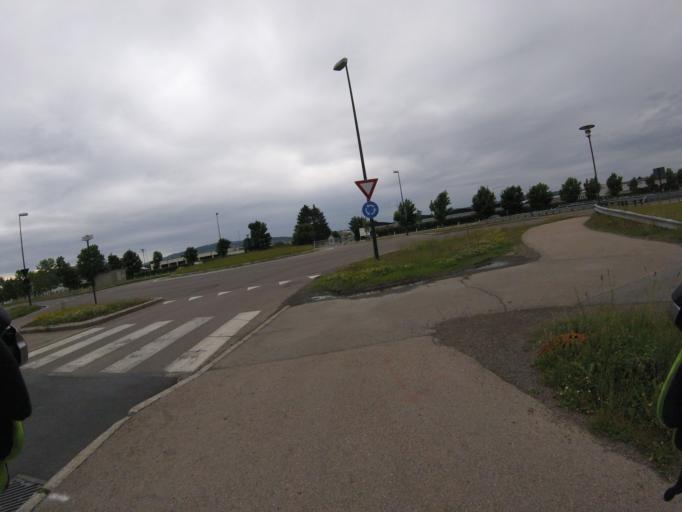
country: NO
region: Akershus
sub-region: Skedsmo
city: Lillestrom
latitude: 59.9729
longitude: 11.0423
